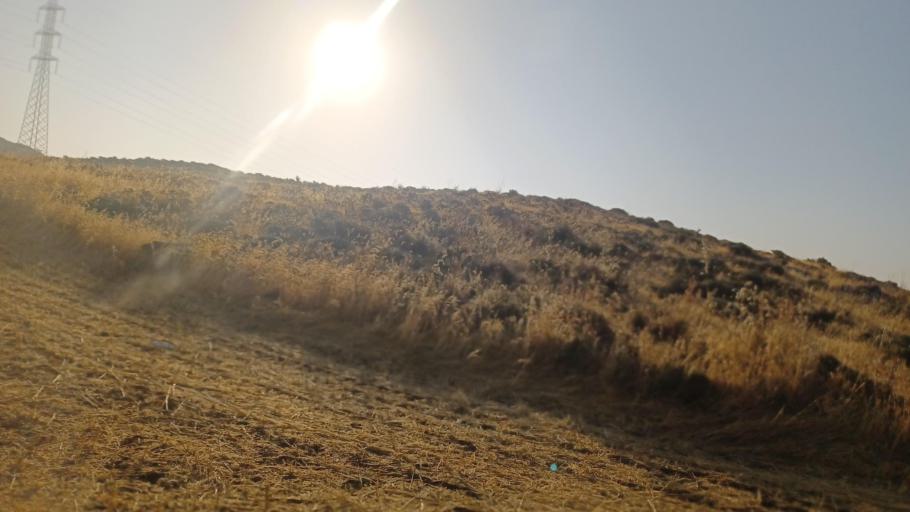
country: CY
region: Larnaka
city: Mosfiloti
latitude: 34.9743
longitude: 33.4316
